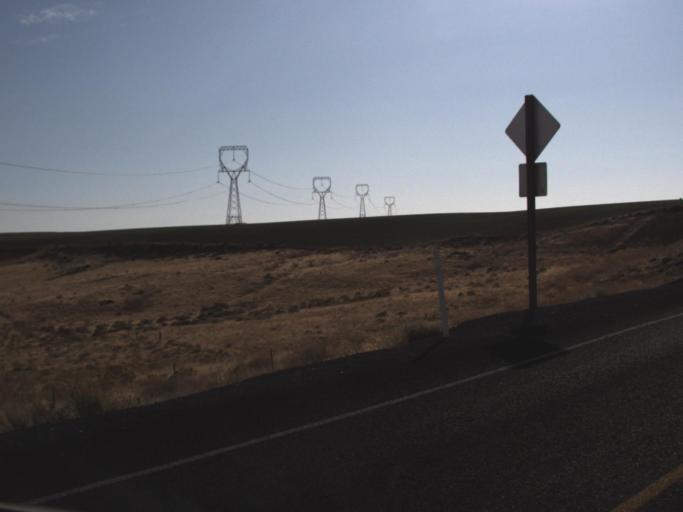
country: US
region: Washington
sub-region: Franklin County
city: Connell
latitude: 46.6261
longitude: -118.7224
